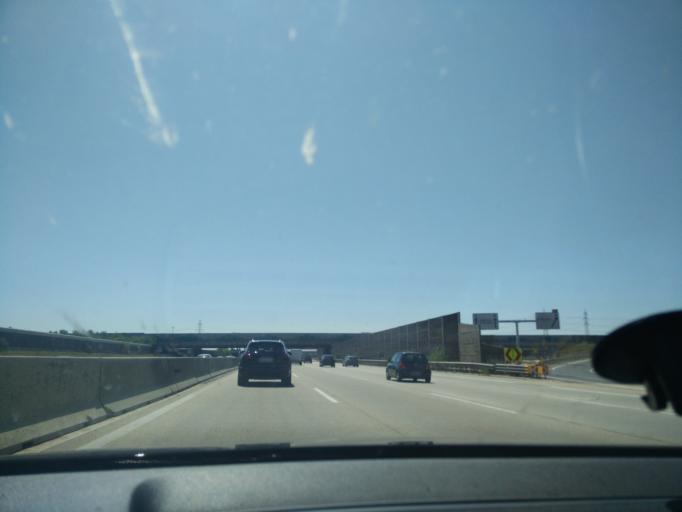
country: AT
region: Lower Austria
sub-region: Politischer Bezirk Modling
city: Biedermannsdorf
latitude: 48.0832
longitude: 16.3332
